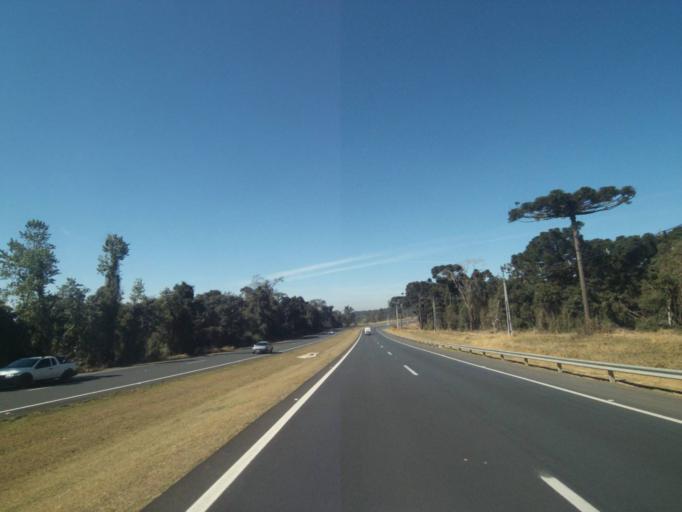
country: BR
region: Parana
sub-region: Carambei
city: Carambei
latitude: -24.9094
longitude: -50.4194
